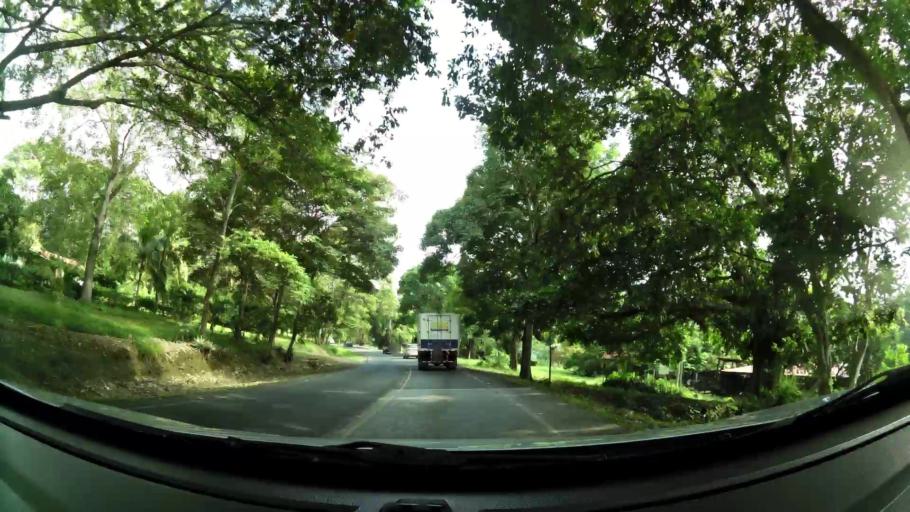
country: CR
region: Guanacaste
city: Juntas
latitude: 10.1851
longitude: -84.9453
